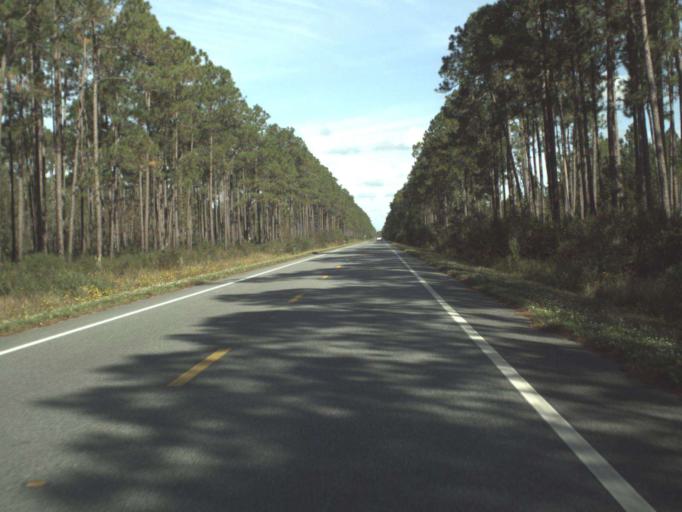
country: US
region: Florida
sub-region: Franklin County
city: Apalachicola
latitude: 29.8656
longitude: -84.9744
